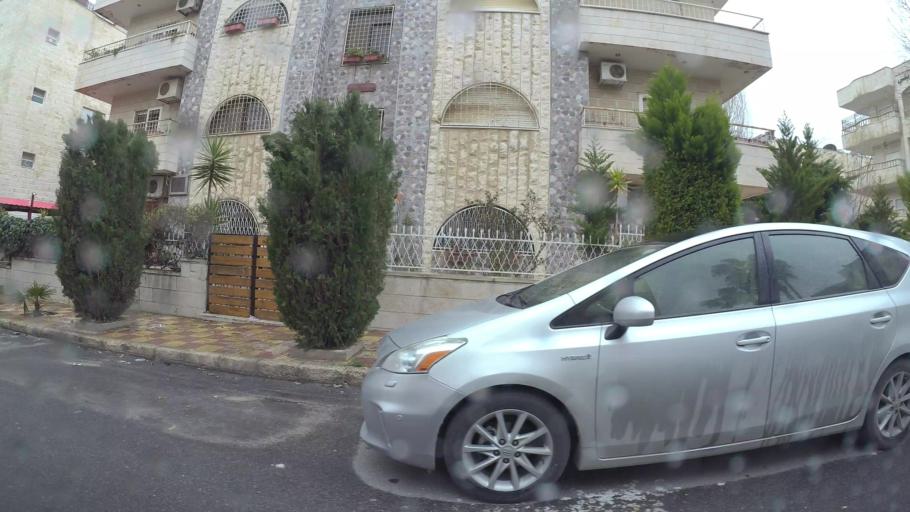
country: JO
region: Amman
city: Al Jubayhah
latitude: 31.9876
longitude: 35.8615
